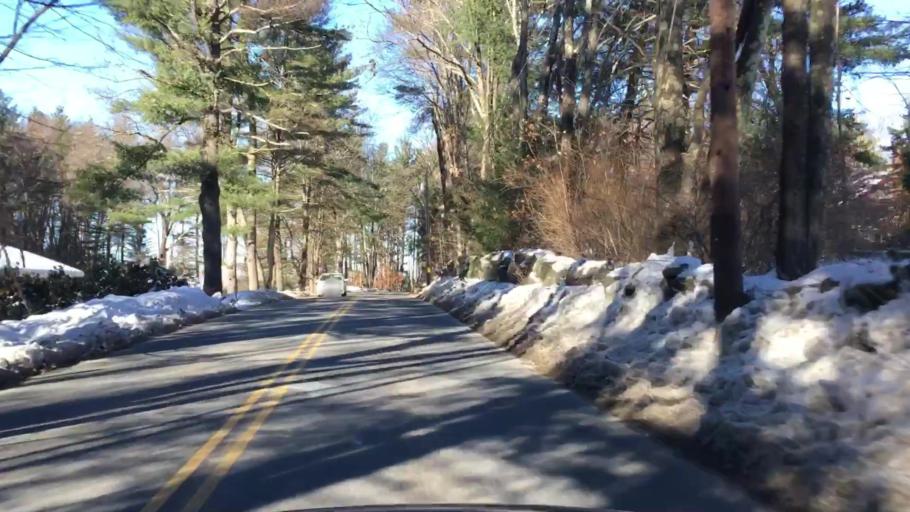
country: US
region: New Hampshire
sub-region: Hillsborough County
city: Milford
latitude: 42.8189
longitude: -71.6332
